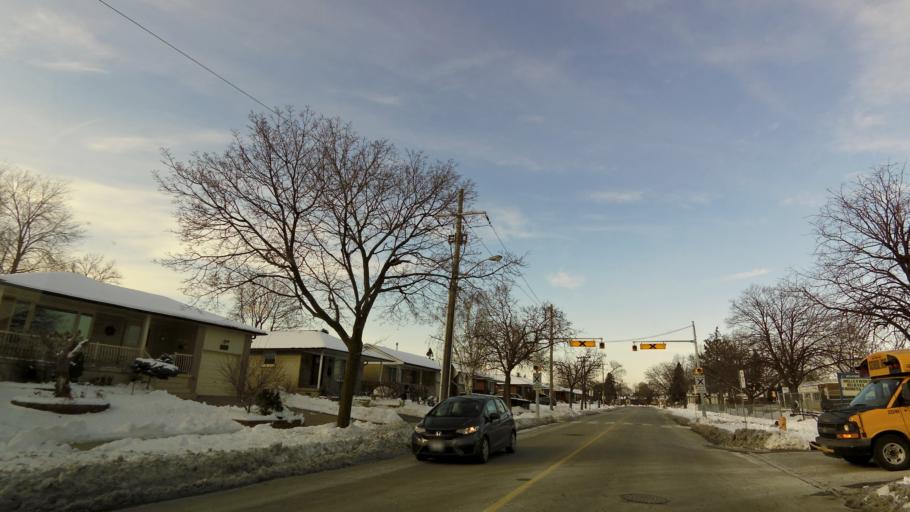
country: CA
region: Ontario
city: Etobicoke
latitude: 43.6556
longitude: -79.5768
